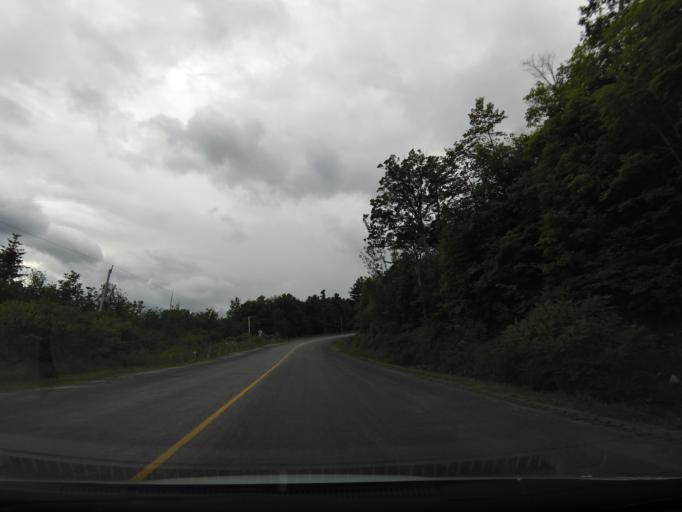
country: CA
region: Ontario
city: Perth
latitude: 44.6425
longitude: -76.5154
